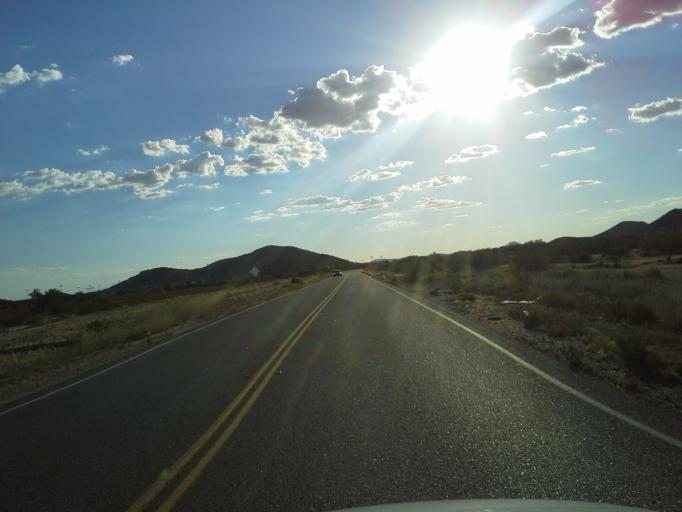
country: US
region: Arizona
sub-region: Maricopa County
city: Cave Creek
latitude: 33.6841
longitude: -112.0091
